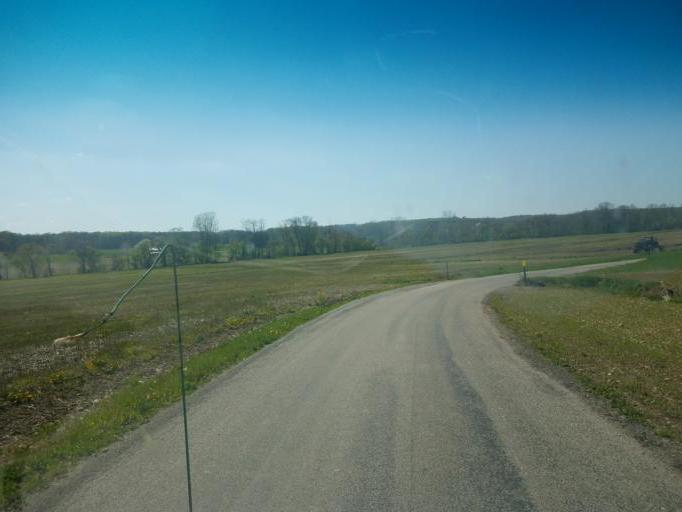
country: US
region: Ohio
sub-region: Medina County
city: Lodi
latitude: 40.9473
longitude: -82.0187
